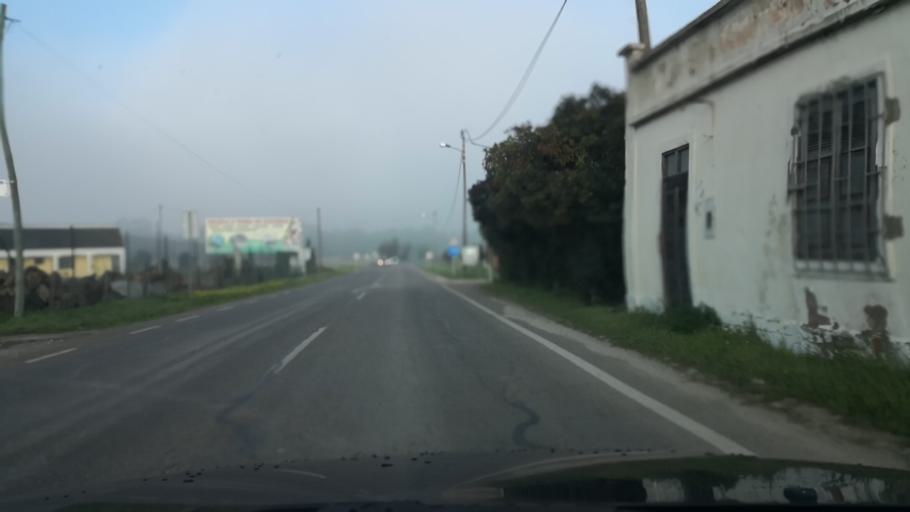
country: PT
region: Setubal
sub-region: Palmela
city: Pinhal Novo
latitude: 38.6035
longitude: -8.9043
